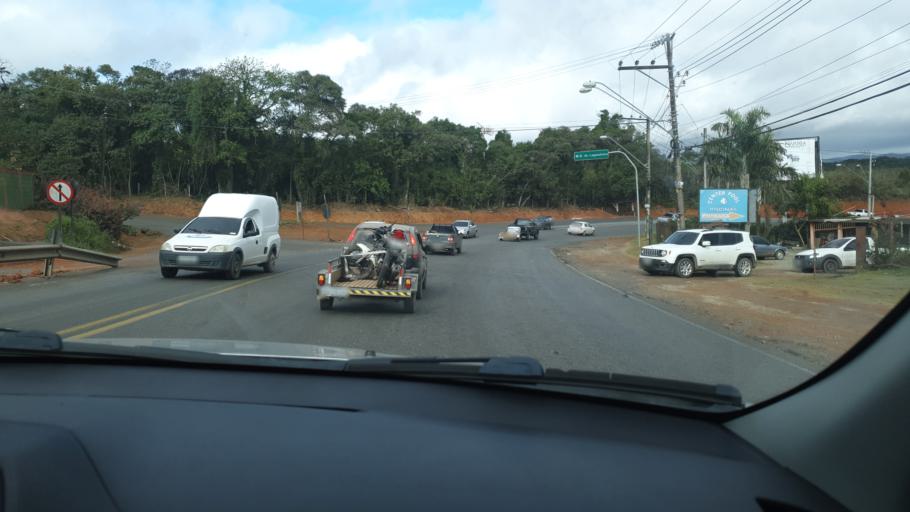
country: BR
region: Sao Paulo
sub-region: Ibiuna
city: Ibiuna
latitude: -23.6635
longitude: -47.1900
